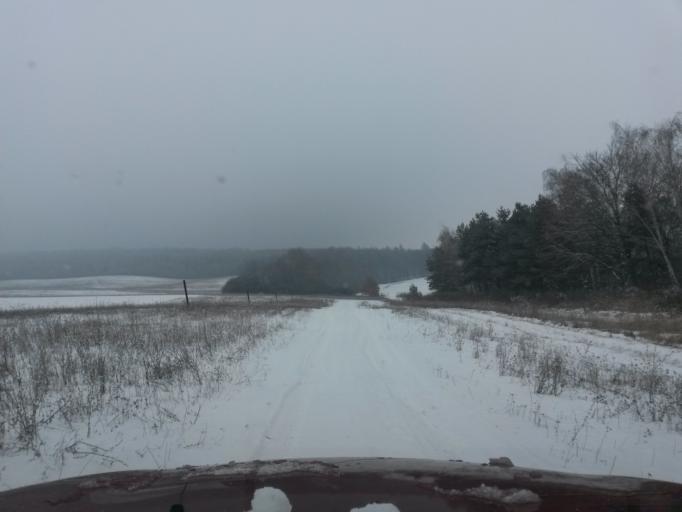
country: SK
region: Kosicky
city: Kosice
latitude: 48.7239
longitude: 21.3260
